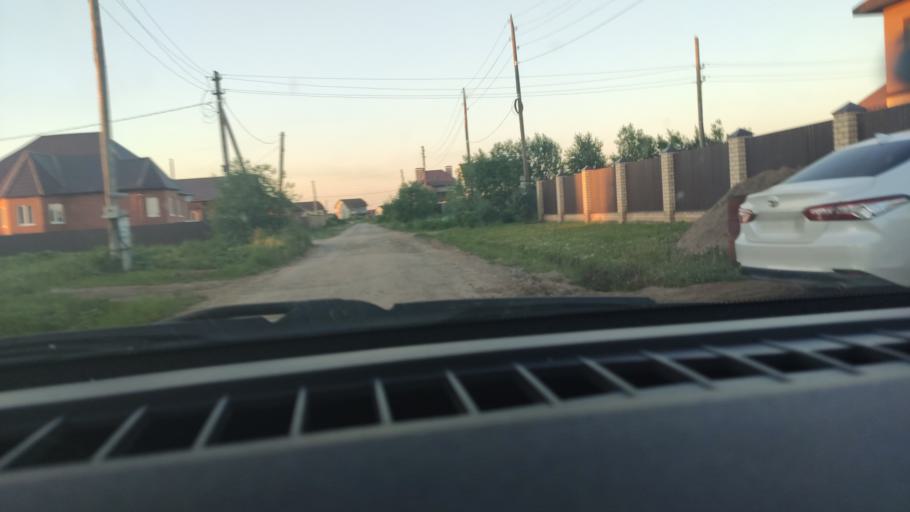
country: RU
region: Perm
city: Kultayevo
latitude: 57.9003
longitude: 55.9687
